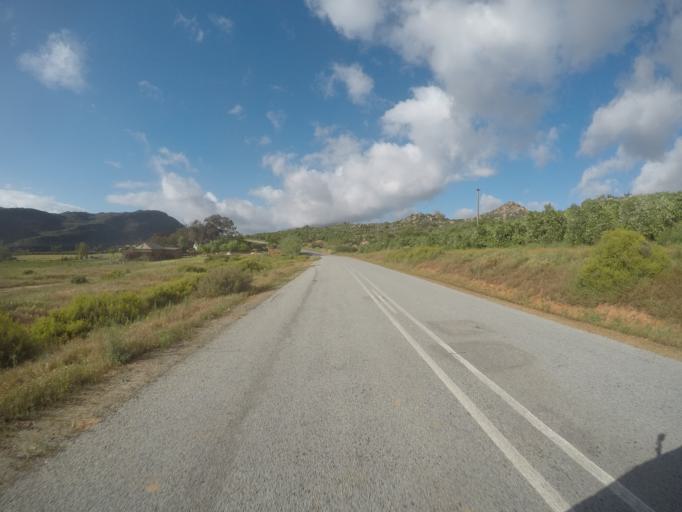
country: ZA
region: Western Cape
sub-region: West Coast District Municipality
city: Clanwilliam
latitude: -32.4348
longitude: 18.9393
